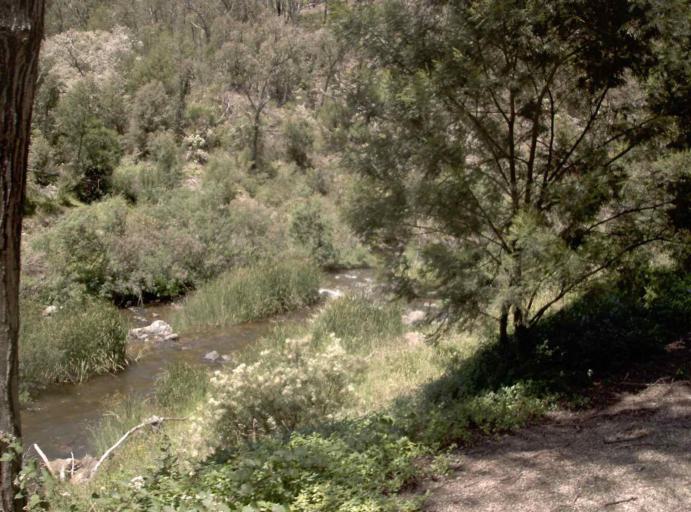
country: AU
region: Victoria
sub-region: East Gippsland
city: Bairnsdale
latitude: -37.4383
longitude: 147.8343
